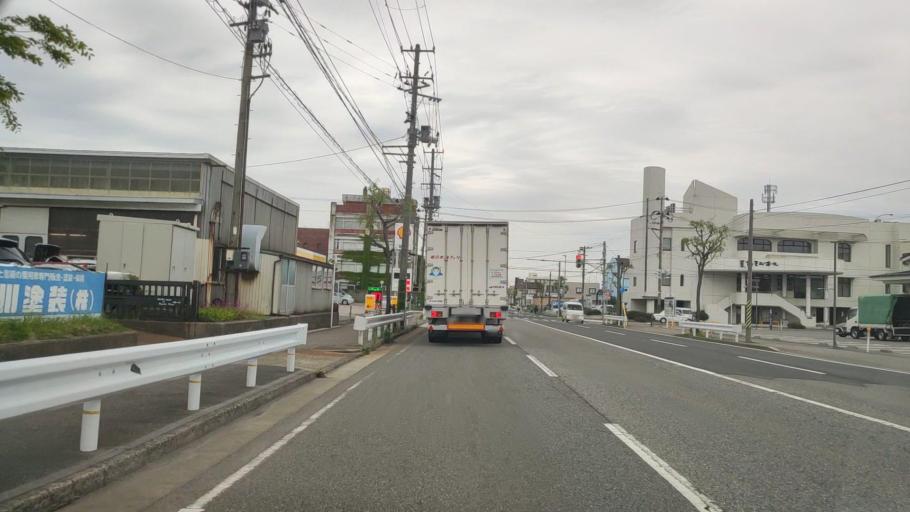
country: JP
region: Niigata
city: Niigata-shi
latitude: 37.9264
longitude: 139.0658
